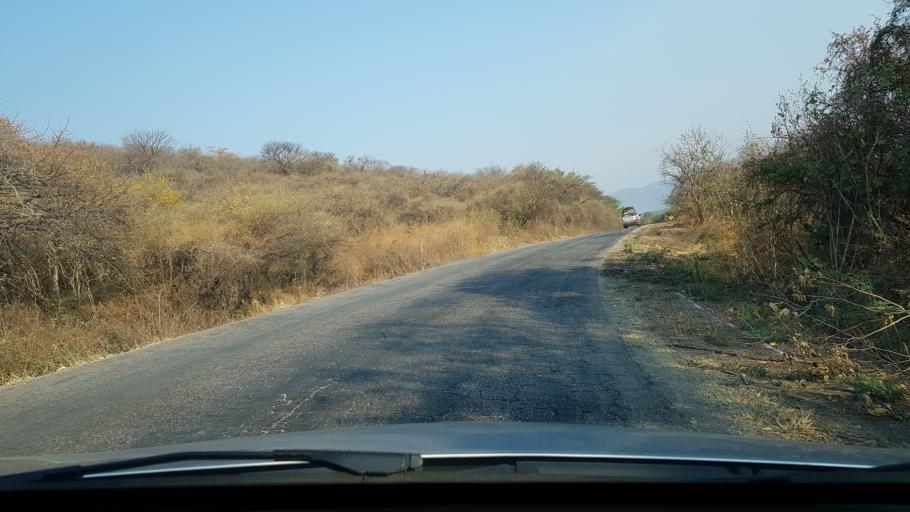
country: MX
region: Morelos
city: Tlaltizapan
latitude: 18.6778
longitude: -99.0864
